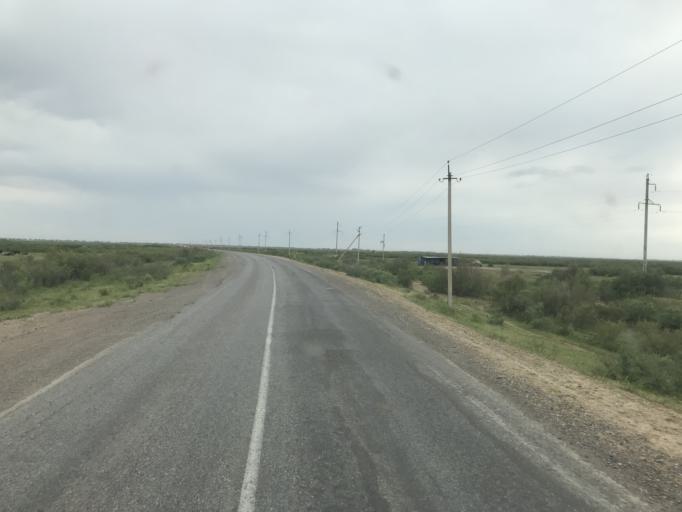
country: KZ
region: Ongtustik Qazaqstan
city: Asykata
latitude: 41.0045
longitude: 68.4725
